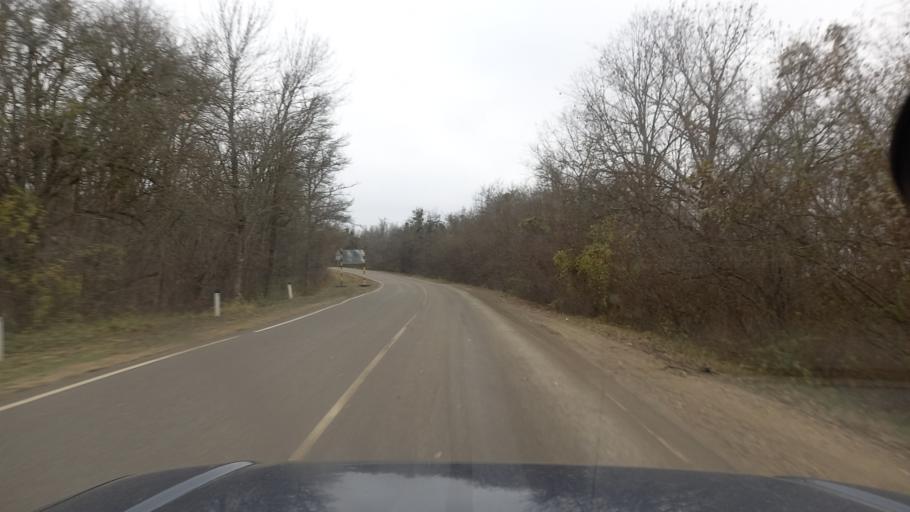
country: RU
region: Krasnodarskiy
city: Goryachiy Klyuch
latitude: 44.5523
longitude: 39.2516
